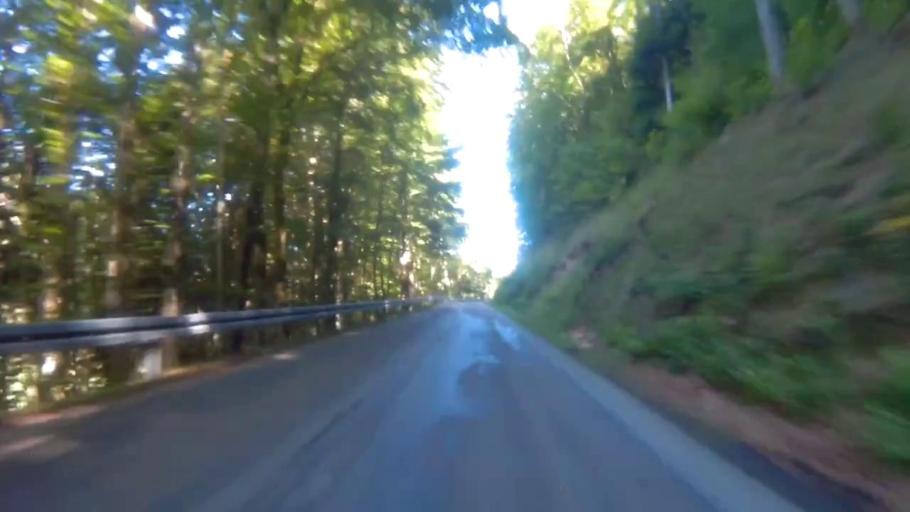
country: DE
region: Baden-Wuerttemberg
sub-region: Freiburg Region
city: Bollen
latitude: 47.7537
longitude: 7.7611
